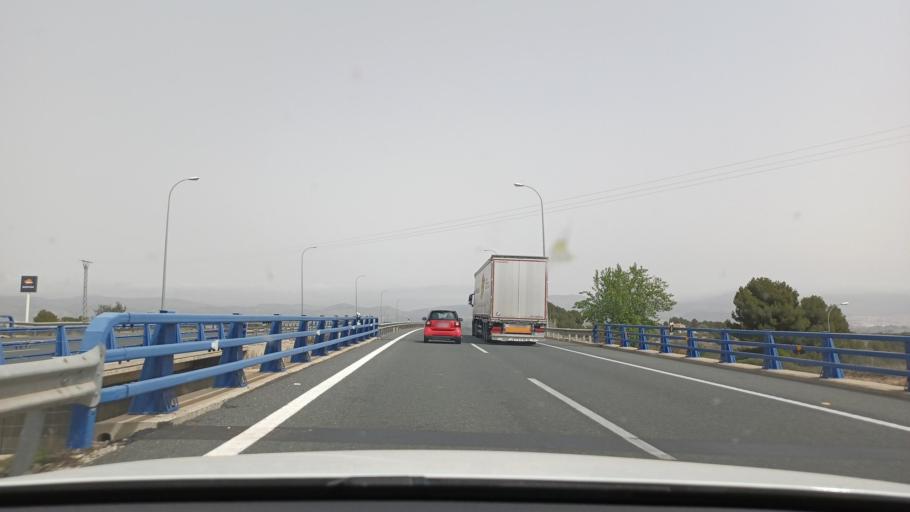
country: ES
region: Valencia
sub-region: Provincia de Alicante
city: Castalla
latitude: 38.5749
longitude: -0.6531
